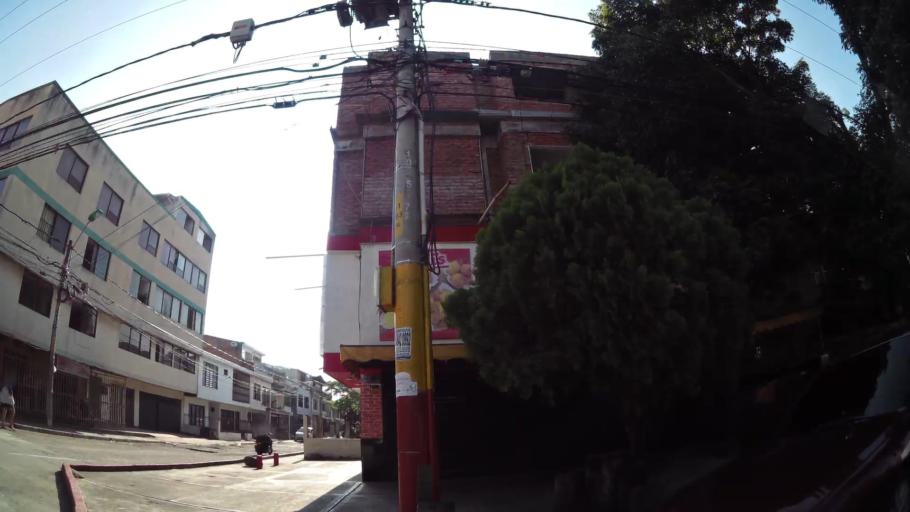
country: CO
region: Valle del Cauca
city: Cali
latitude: 3.4181
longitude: -76.5348
